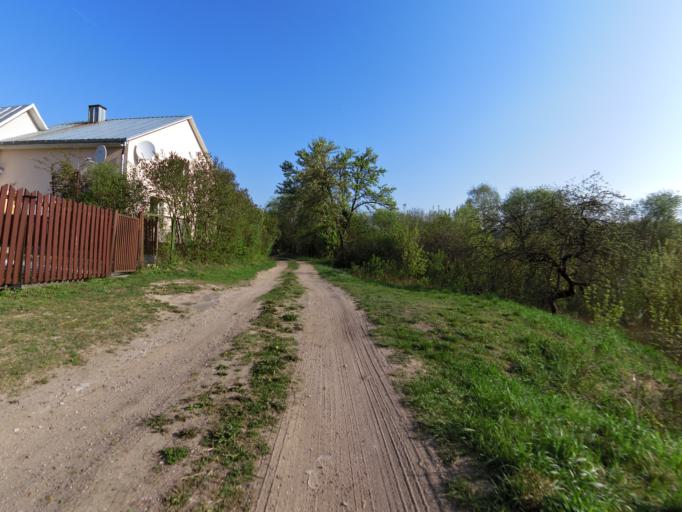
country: LT
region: Vilnius County
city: Vilkpede
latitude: 54.6737
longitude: 25.2290
